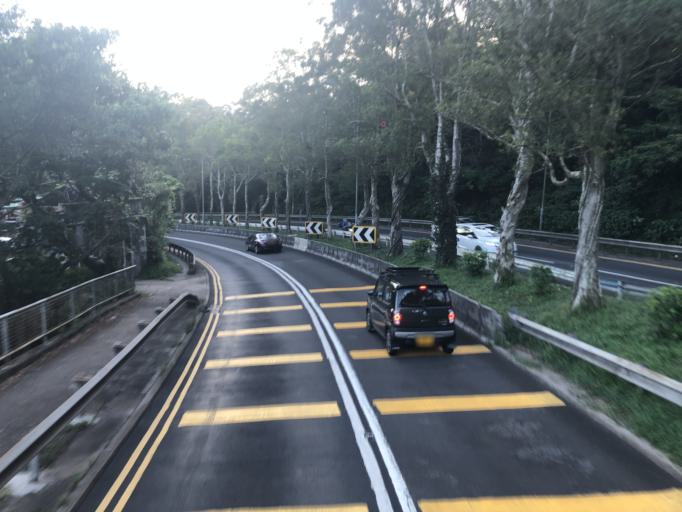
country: HK
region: Sai Kung
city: Sai Kung
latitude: 22.3382
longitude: 114.2442
